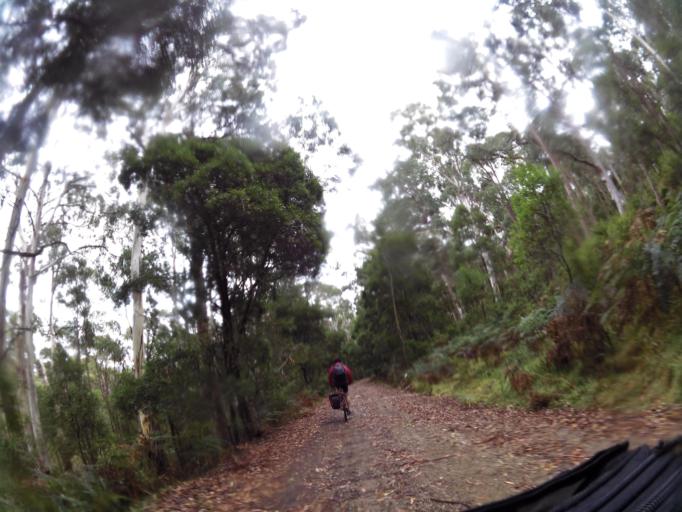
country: AU
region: New South Wales
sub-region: Greater Hume Shire
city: Holbrook
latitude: -36.1922
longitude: 147.5091
